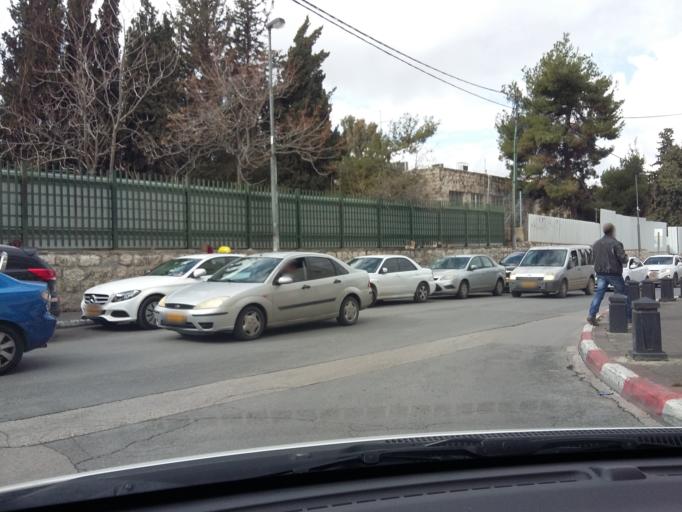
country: PS
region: West Bank
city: East Jerusalem
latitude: 31.7868
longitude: 35.2320
